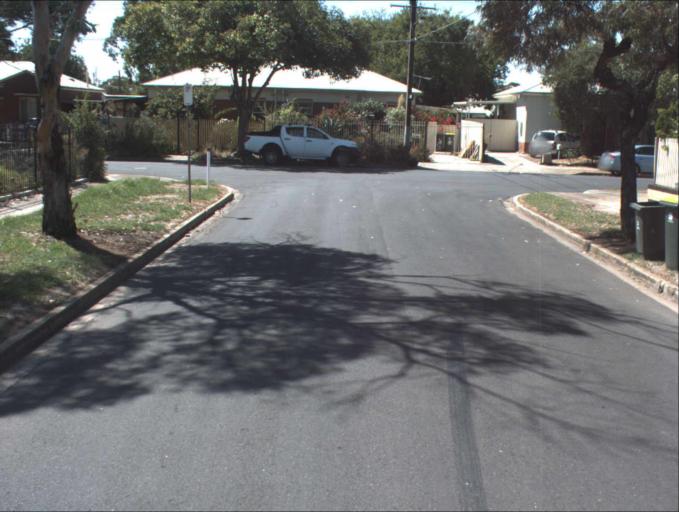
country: AU
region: South Australia
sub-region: Port Adelaide Enfield
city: Blair Athol
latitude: -34.8584
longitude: 138.5844
